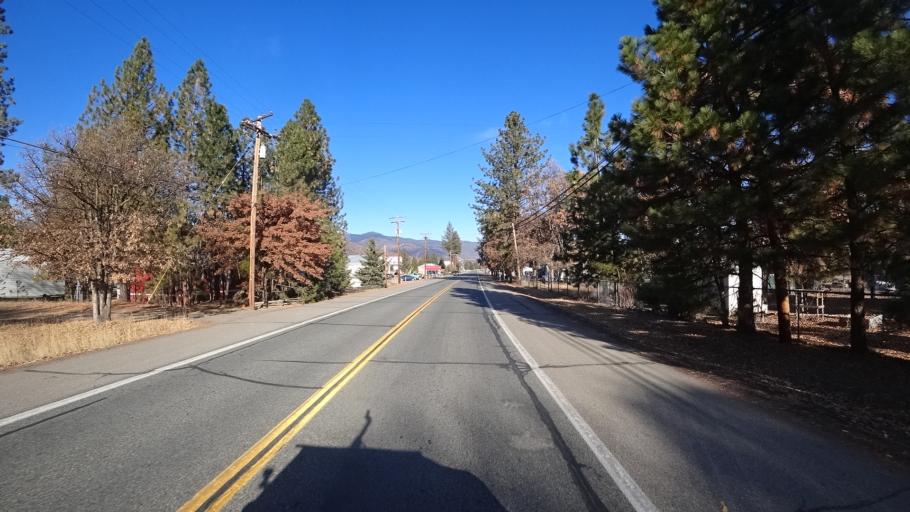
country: US
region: California
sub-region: Siskiyou County
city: Yreka
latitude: 41.6882
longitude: -122.6354
